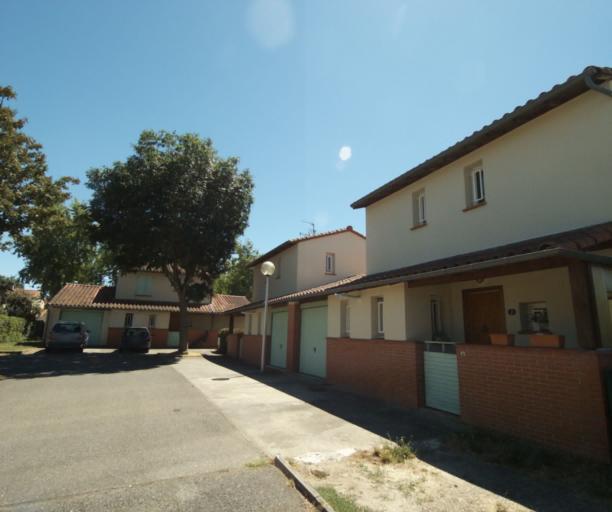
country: FR
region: Midi-Pyrenees
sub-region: Departement de la Haute-Garonne
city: Pechabou
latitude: 43.5133
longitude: 1.5115
